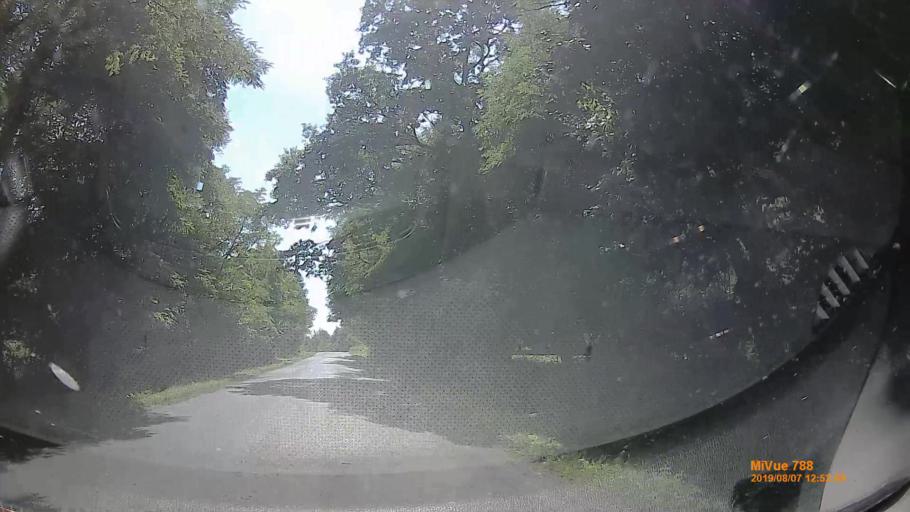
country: HU
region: Zala
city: Cserszegtomaj
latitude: 46.8414
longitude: 17.2678
